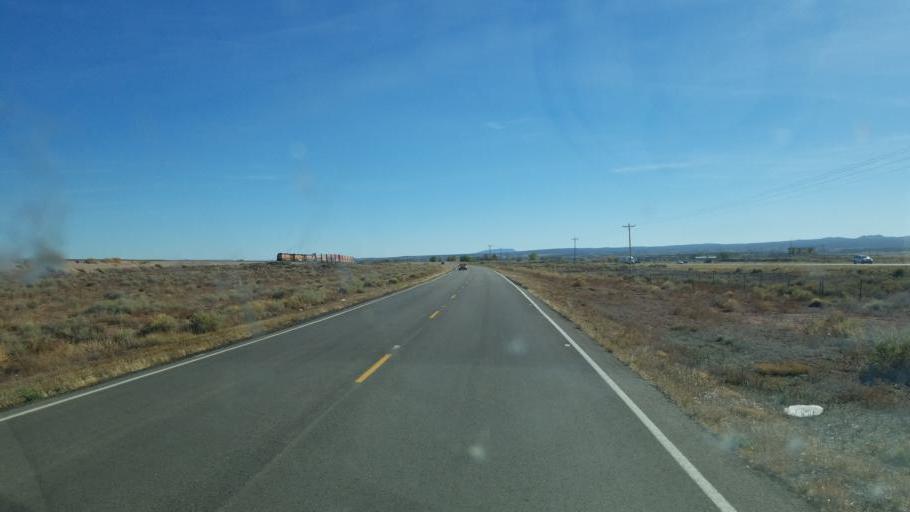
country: US
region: New Mexico
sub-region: Cibola County
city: Milan
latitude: 35.2895
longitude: -107.9862
